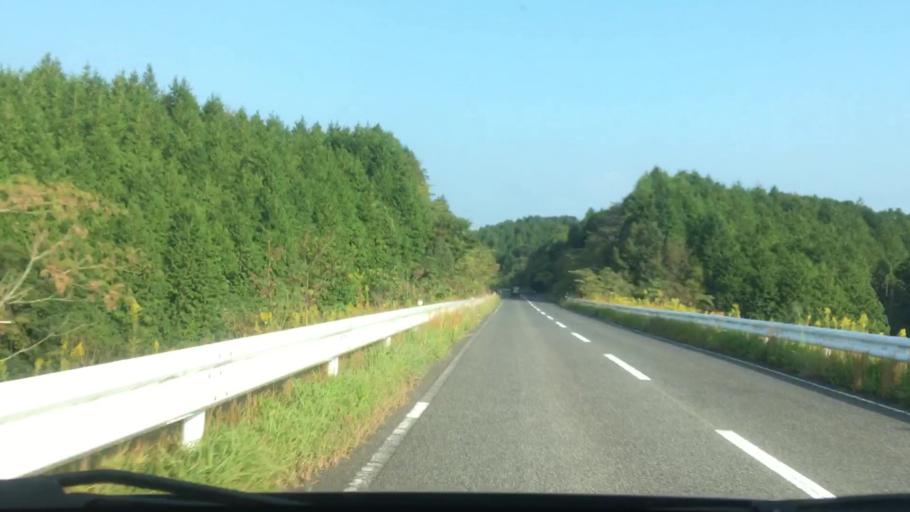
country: JP
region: Nagasaki
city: Sasebo
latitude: 33.0217
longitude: 129.6989
